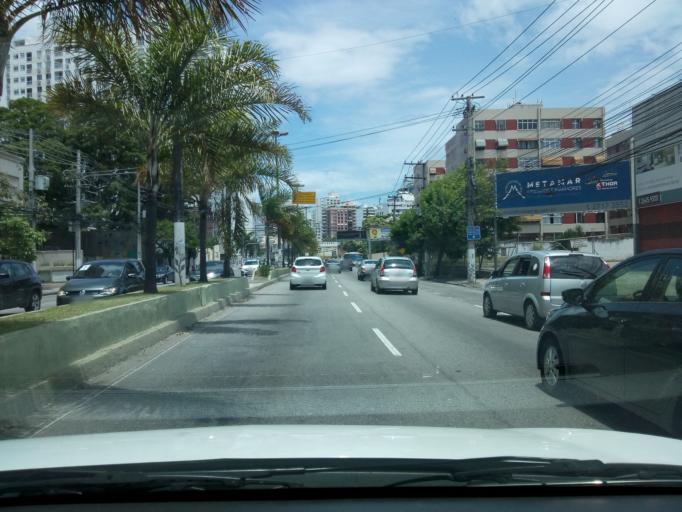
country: BR
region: Rio de Janeiro
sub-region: Niteroi
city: Niteroi
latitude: -22.8968
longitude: -43.1123
